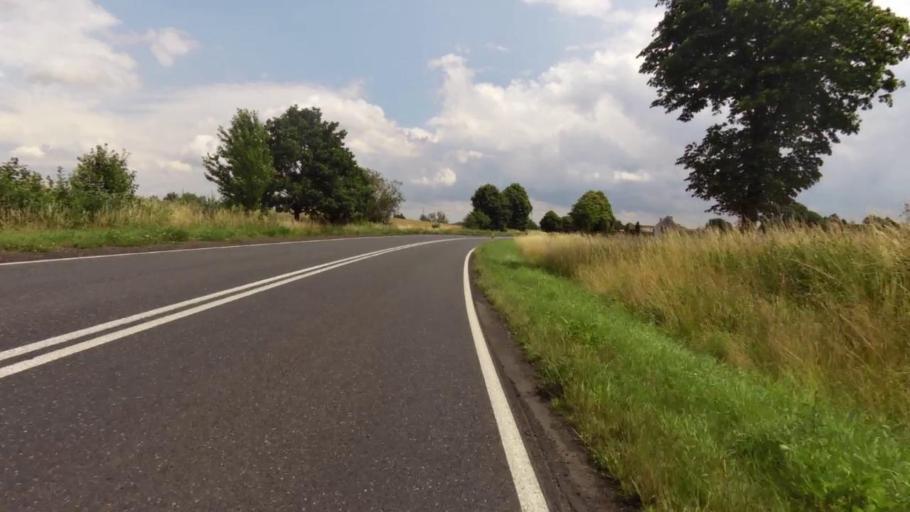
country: PL
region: West Pomeranian Voivodeship
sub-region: Powiat mysliborski
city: Nowogrodek Pomorski
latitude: 52.9939
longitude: 15.0900
